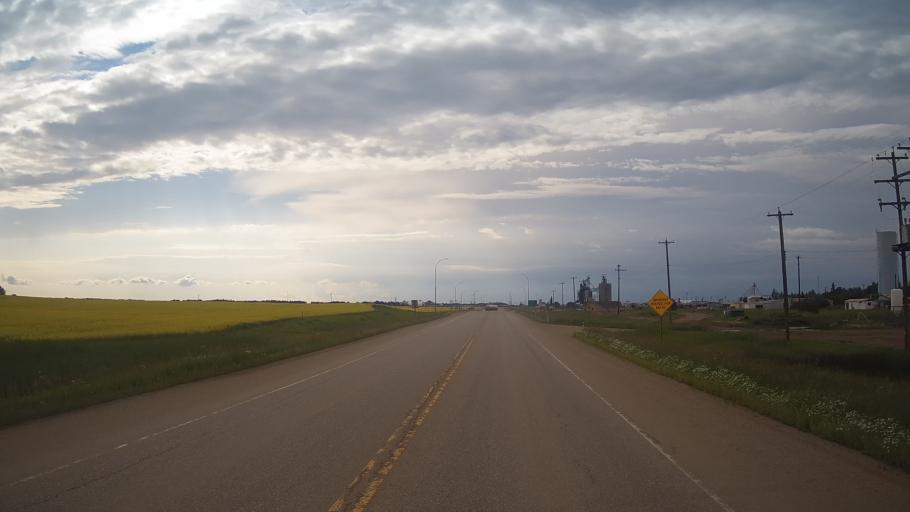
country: CA
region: Alberta
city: Viking
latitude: 53.0907
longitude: -111.7770
